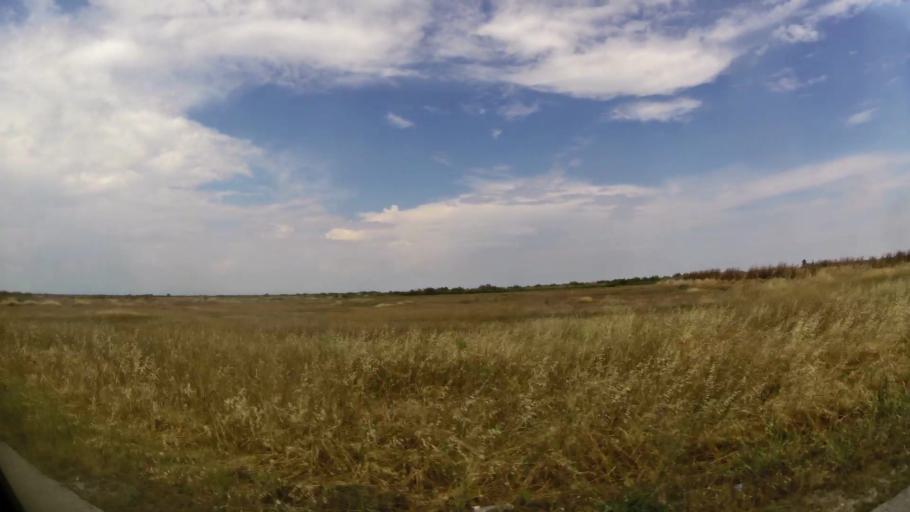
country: GR
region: Central Macedonia
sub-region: Nomos Pierias
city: Korinos
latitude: 40.3222
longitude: 22.6223
